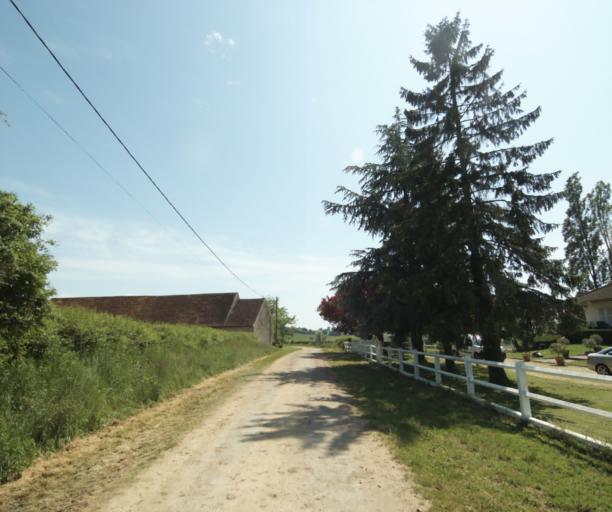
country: FR
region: Bourgogne
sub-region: Departement de Saone-et-Loire
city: Palinges
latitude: 46.5751
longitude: 4.1628
